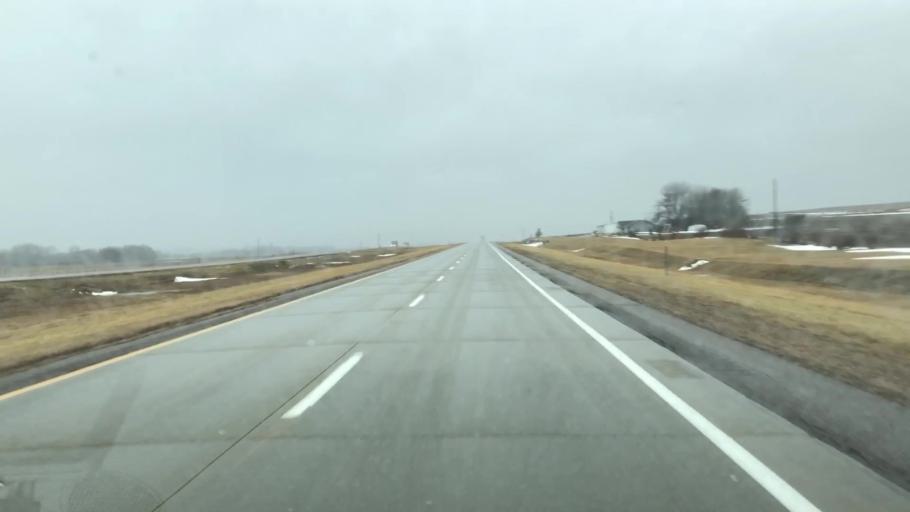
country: US
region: Iowa
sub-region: Sioux County
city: Orange City
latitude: 42.9020
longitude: -96.0853
